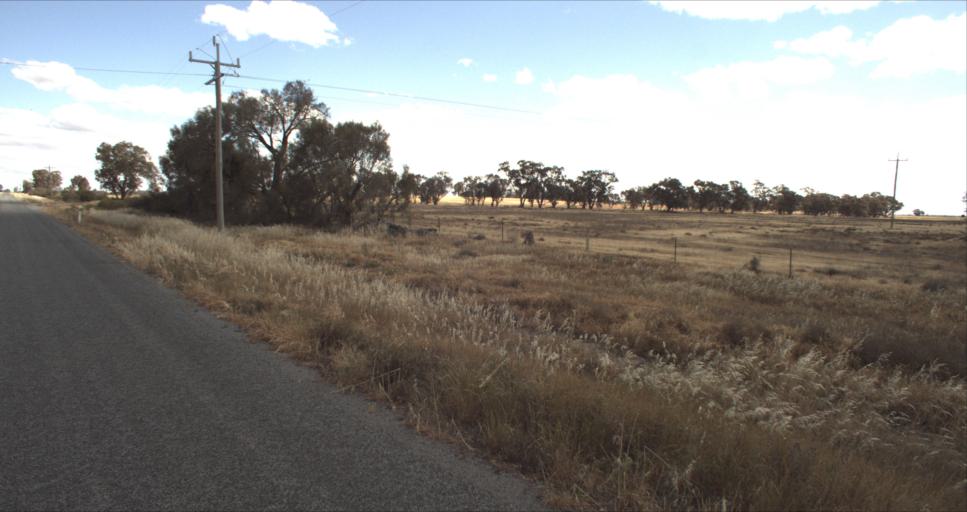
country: AU
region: New South Wales
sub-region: Leeton
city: Leeton
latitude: -34.4870
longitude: 146.2480
